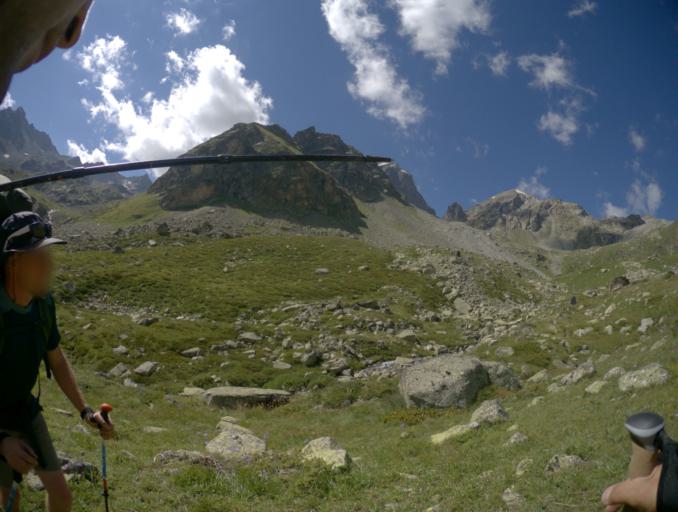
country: RU
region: Karachayevo-Cherkesiya
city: Uchkulan
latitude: 43.3253
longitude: 42.1038
